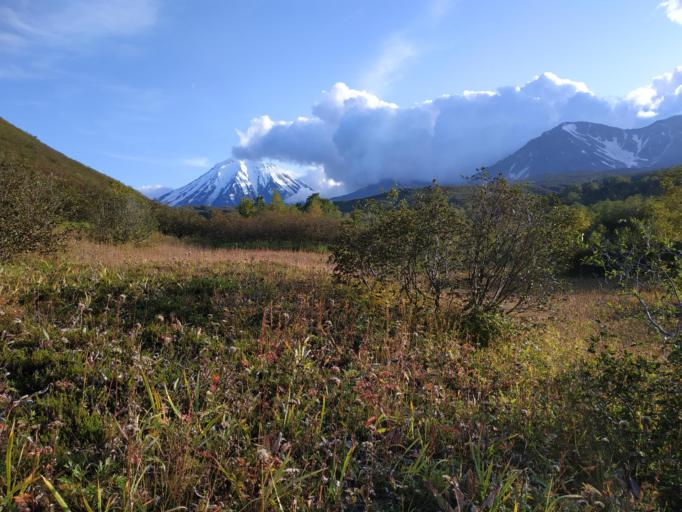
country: RU
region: Kamtsjatka
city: Petropavlovsk-Kamchatsky
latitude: 53.4457
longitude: 158.7257
